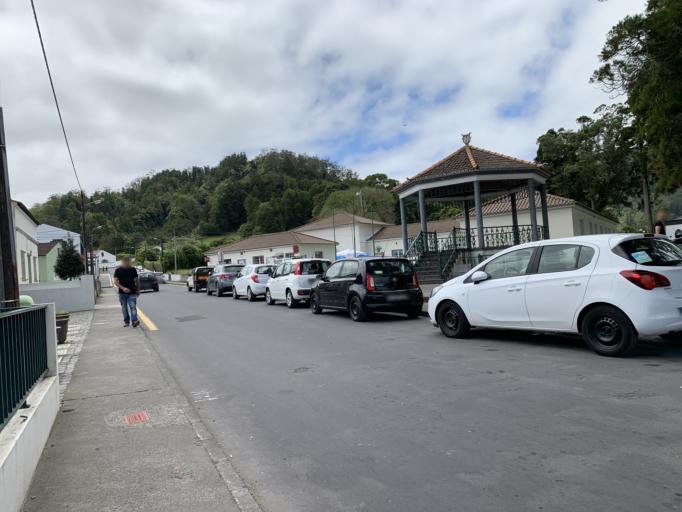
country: PT
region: Azores
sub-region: Ponta Delgada
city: Arrifes
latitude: 37.8629
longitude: -25.7969
